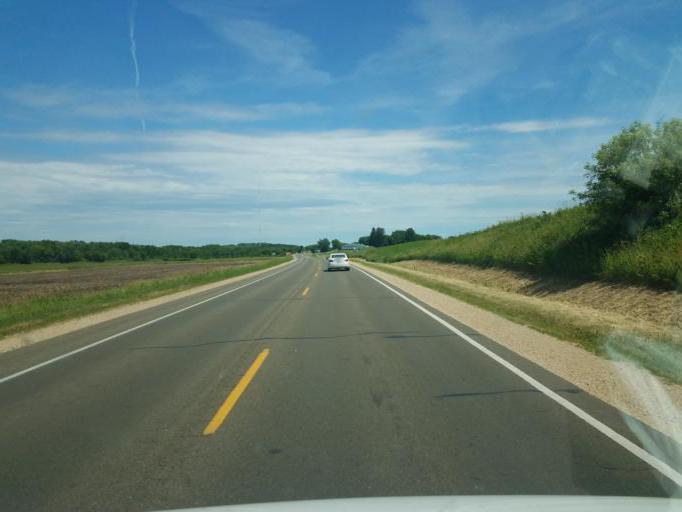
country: US
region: Wisconsin
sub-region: Sauk County
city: Reedsburg
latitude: 43.5431
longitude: -90.0445
